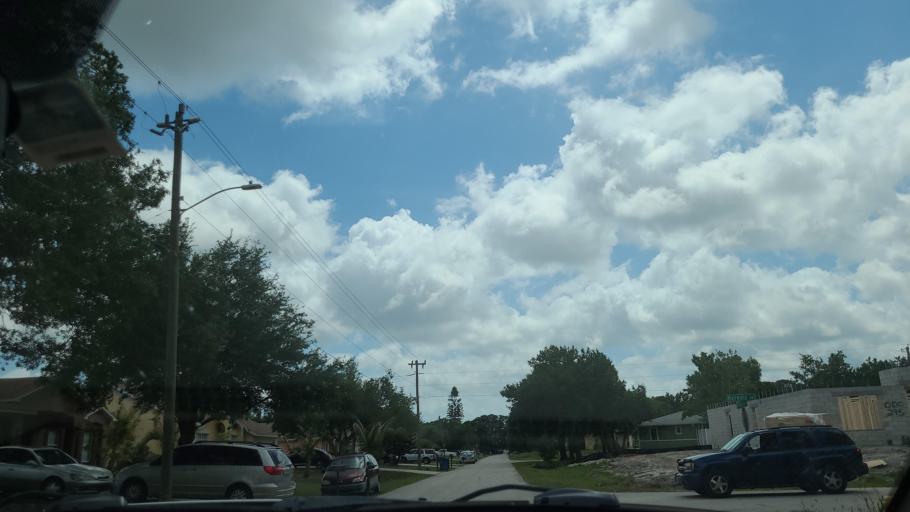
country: US
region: Florida
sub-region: Brevard County
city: June Park
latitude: 28.0058
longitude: -80.6802
